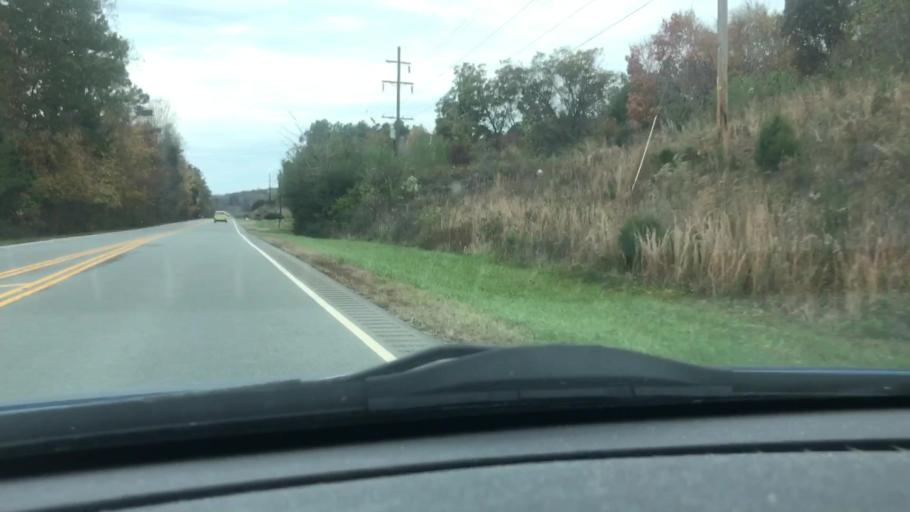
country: US
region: North Carolina
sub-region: Davidson County
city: Thomasville
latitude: 35.7596
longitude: -80.0579
